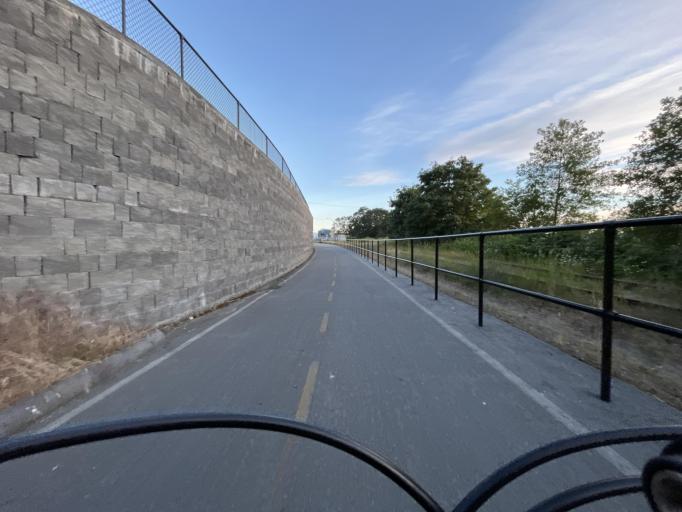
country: CA
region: British Columbia
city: Colwood
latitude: 48.4414
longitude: -123.4294
